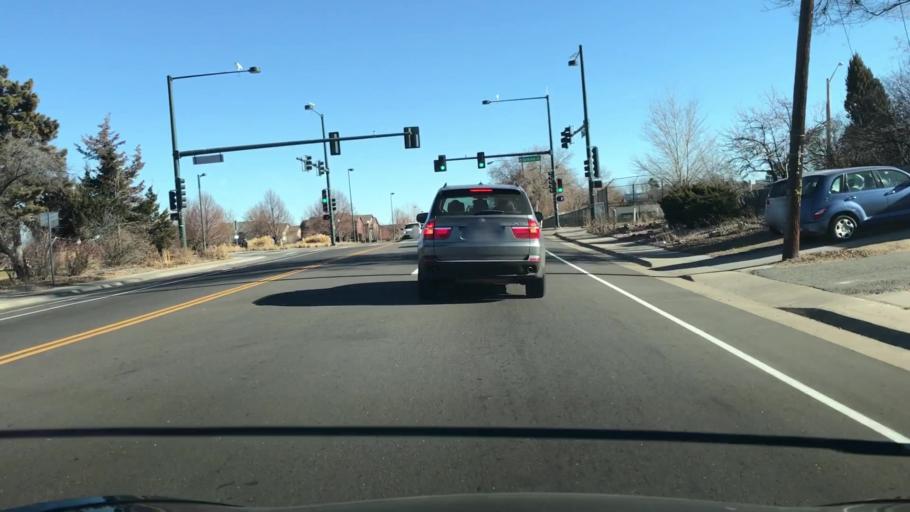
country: US
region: Colorado
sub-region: Arapahoe County
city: Glendale
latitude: 39.7474
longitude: -104.8995
